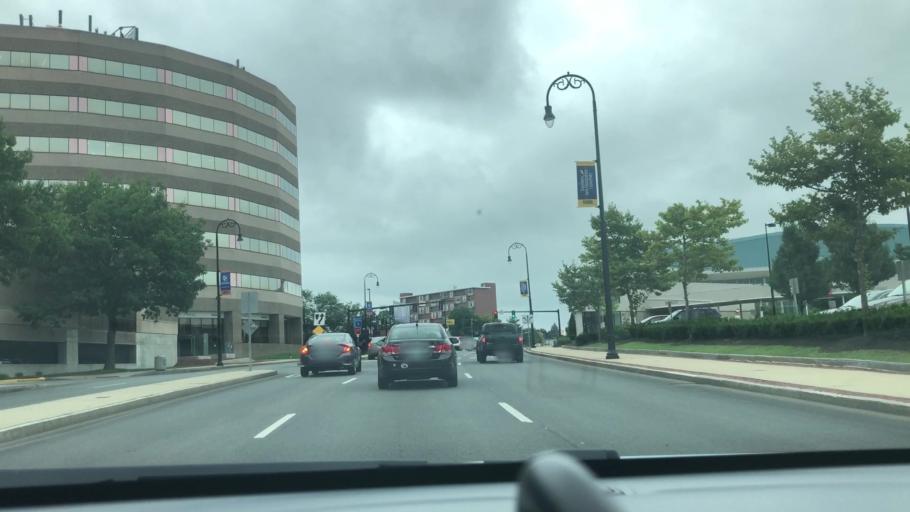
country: US
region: New Hampshire
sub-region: Hillsborough County
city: Manchester
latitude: 42.9871
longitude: -71.4647
